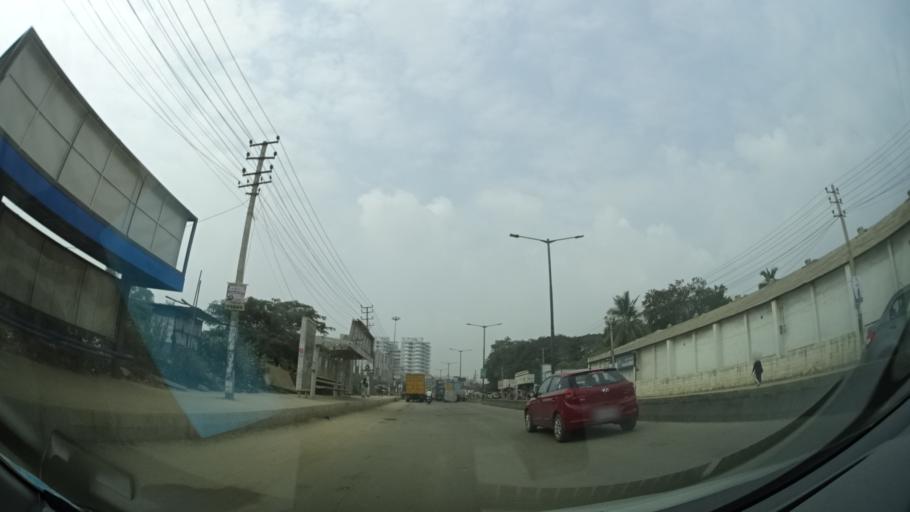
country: IN
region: Karnataka
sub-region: Bangalore Rural
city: Hoskote
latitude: 12.9835
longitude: 77.7538
